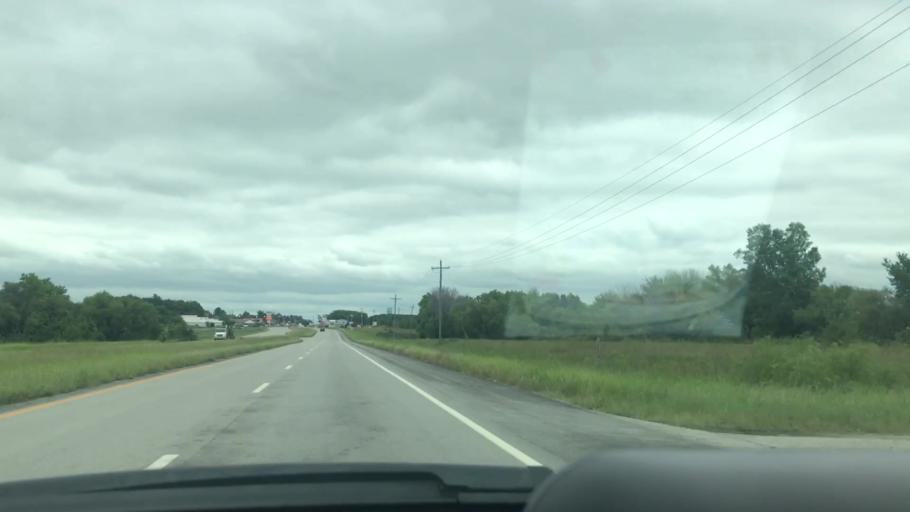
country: US
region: Oklahoma
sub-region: Mayes County
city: Pryor
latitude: 36.4282
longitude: -95.2747
